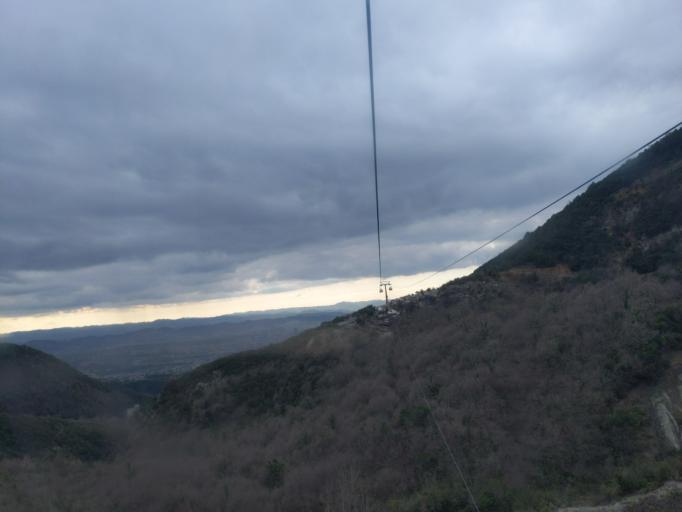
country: AL
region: Tirane
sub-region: Rrethi i Tiranes
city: Dajt
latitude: 41.3639
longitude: 19.8942
